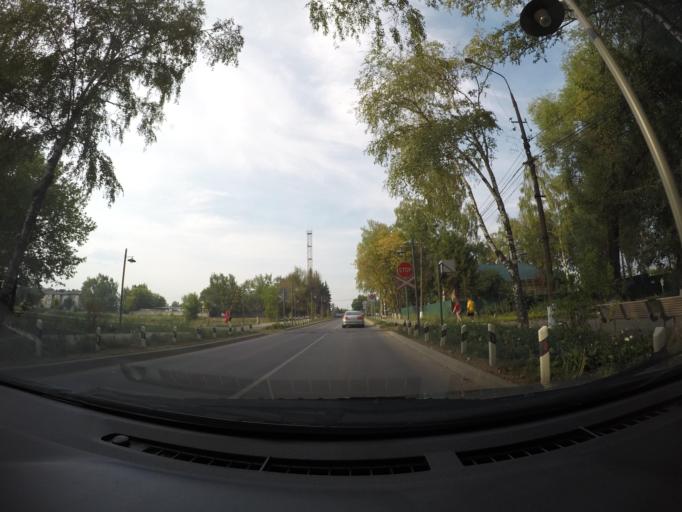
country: RU
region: Moskovskaya
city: Rechitsy
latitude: 55.5874
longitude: 38.5039
